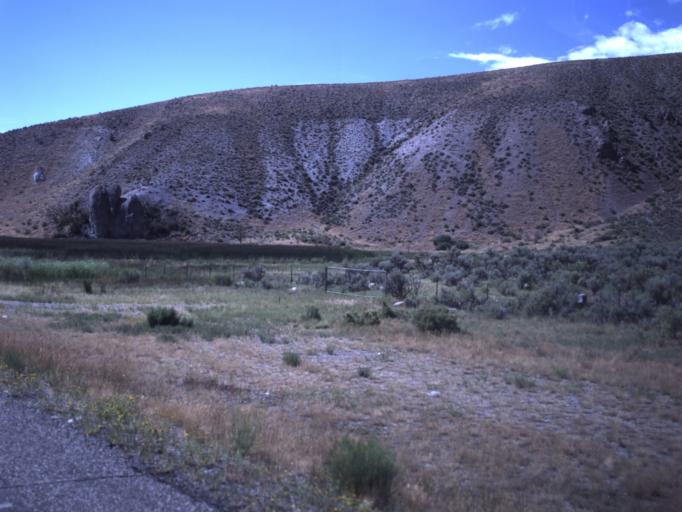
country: US
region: Utah
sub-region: Sevier County
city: Monroe
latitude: 38.4803
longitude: -112.2433
